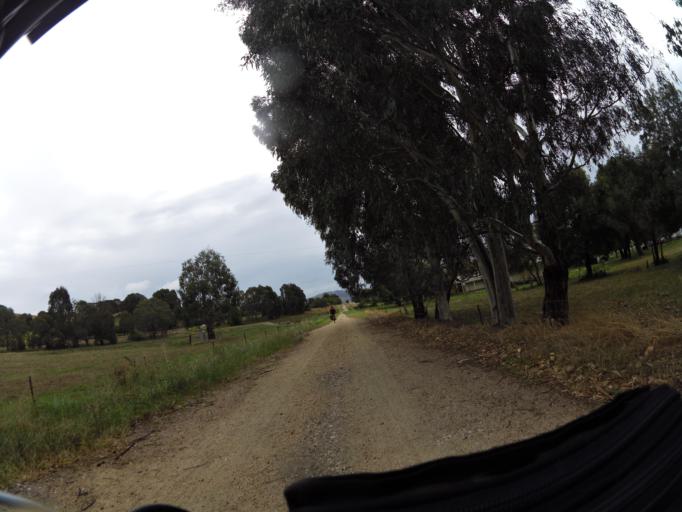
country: AU
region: New South Wales
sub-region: Albury Municipality
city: East Albury
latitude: -36.2252
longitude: 147.0754
